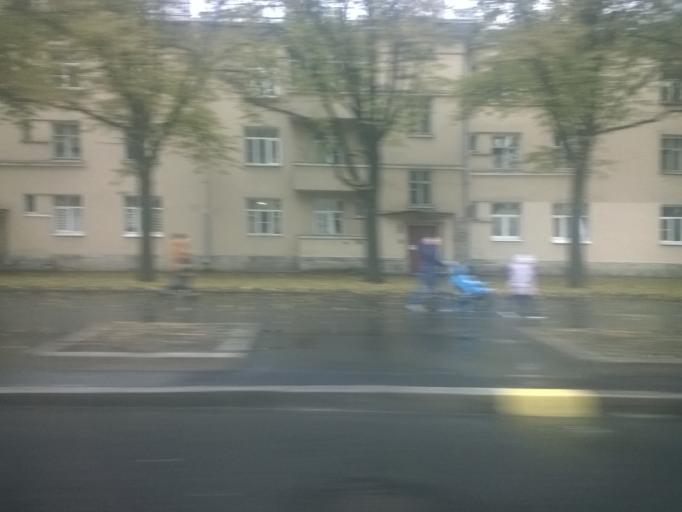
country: RU
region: St.-Petersburg
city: Avtovo
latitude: 59.8890
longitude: 30.2700
